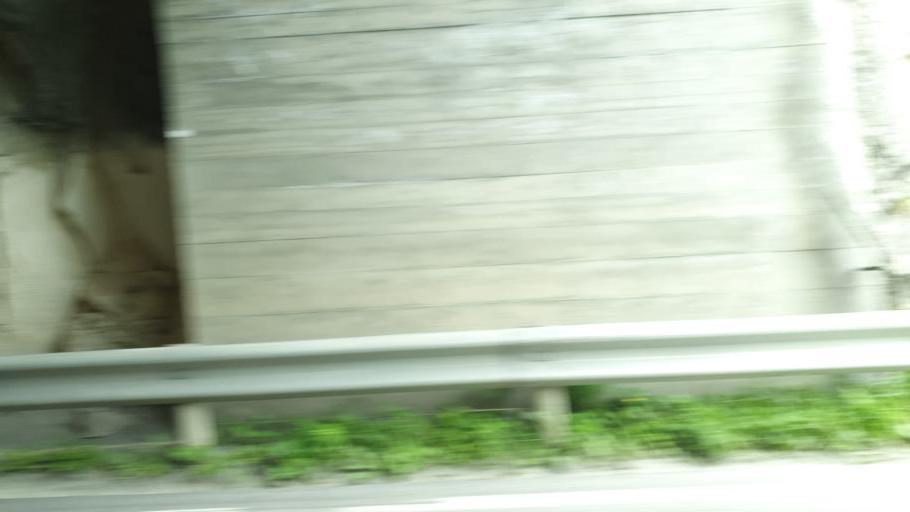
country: NO
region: Sor-Trondelag
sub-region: Trondheim
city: Trondheim
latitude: 63.5929
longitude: 10.4432
